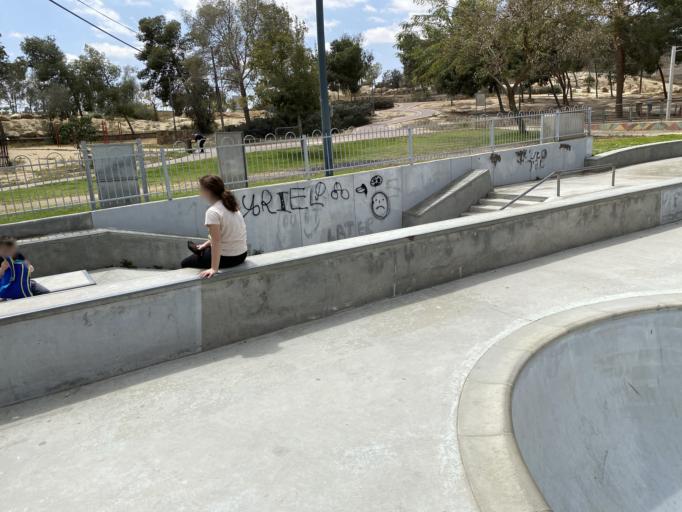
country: IL
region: Southern District
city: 'Arad
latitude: 31.2564
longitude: 35.2150
